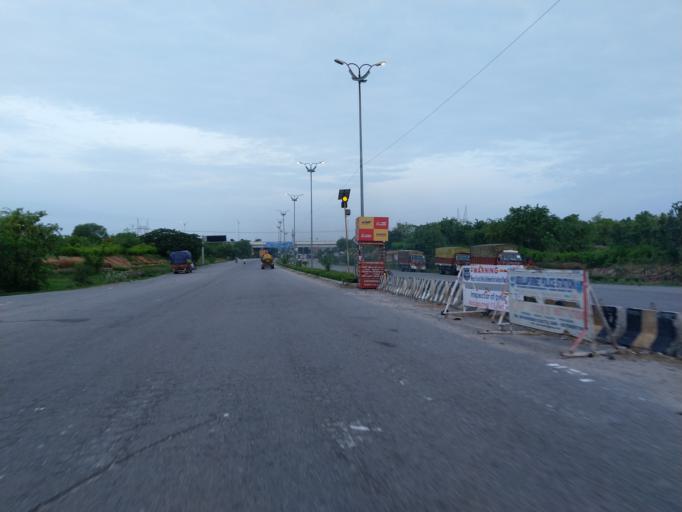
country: IN
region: Telangana
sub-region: Rangareddi
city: Lal Bahadur Nagar
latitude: 17.3173
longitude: 78.6609
